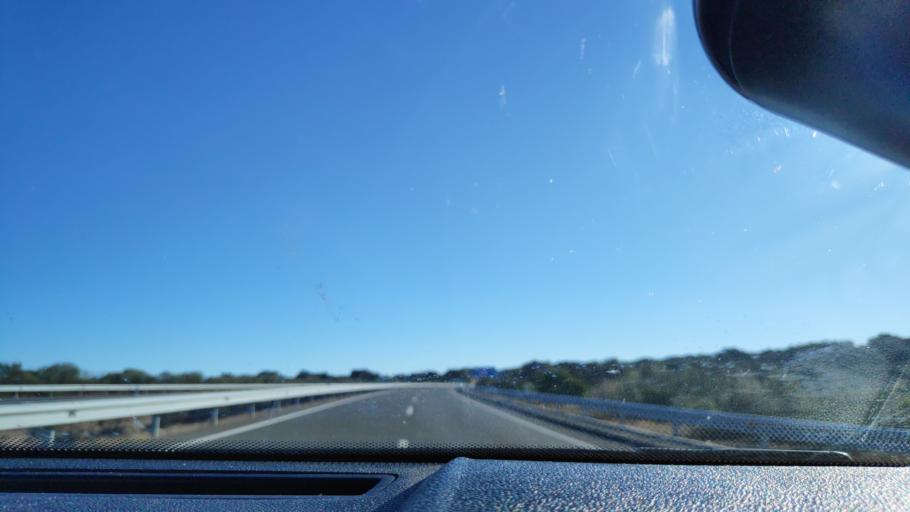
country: ES
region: Extremadura
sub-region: Provincia de Badajoz
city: Monesterio
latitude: 38.1211
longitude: -6.2690
